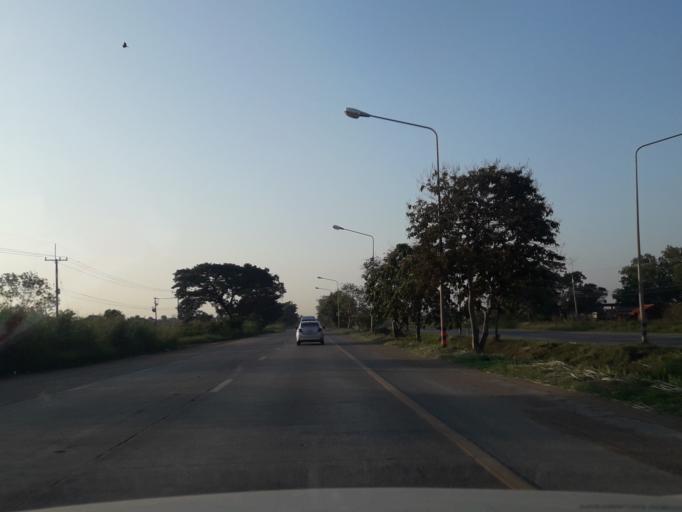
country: TH
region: Phra Nakhon Si Ayutthaya
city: Bang Pa-in
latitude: 14.2448
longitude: 100.5371
